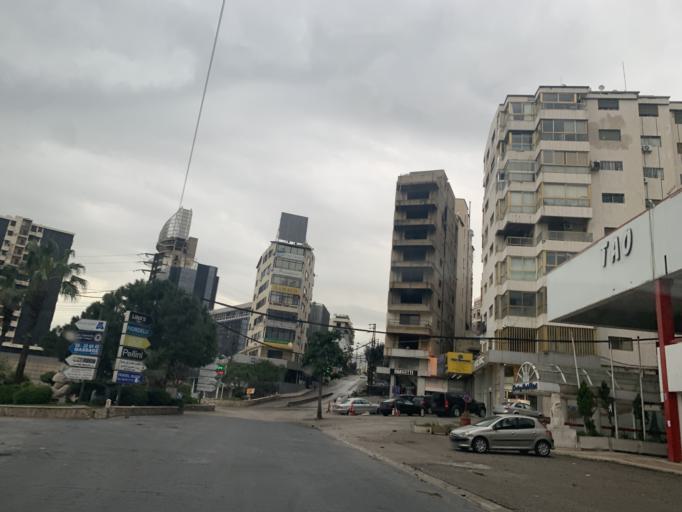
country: LB
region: Mont-Liban
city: Djounie
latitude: 33.9769
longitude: 35.6148
